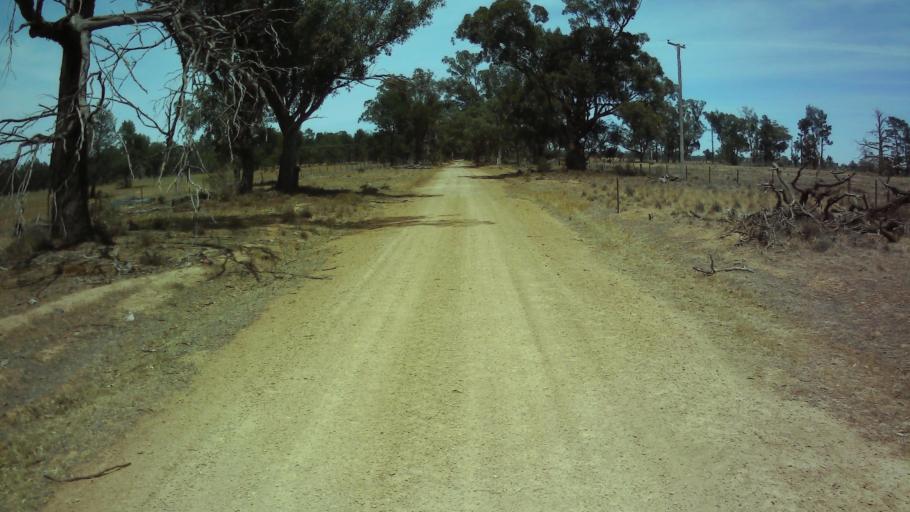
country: AU
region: New South Wales
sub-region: Weddin
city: Grenfell
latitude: -34.0291
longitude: 147.9386
